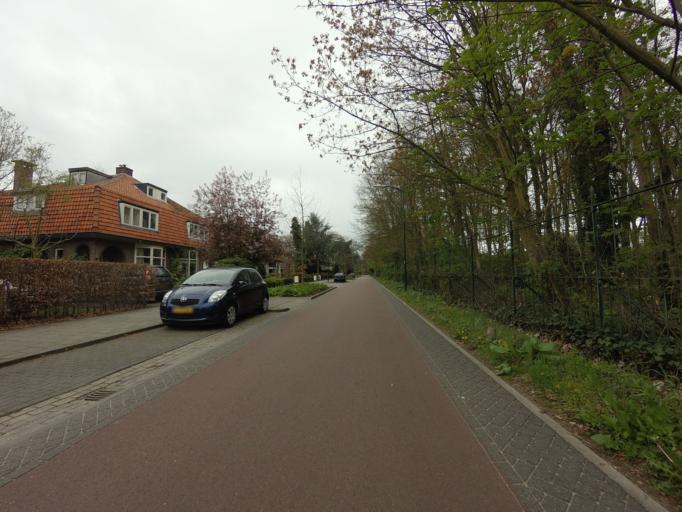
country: NL
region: Utrecht
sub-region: Gemeente Utrechtse Heuvelrug
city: Driebergen-Rijsenburg
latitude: 52.0495
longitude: 5.2829
